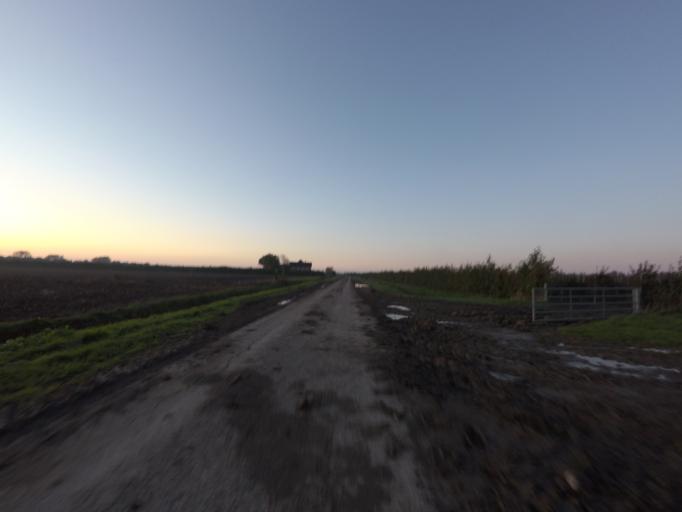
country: NL
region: North Brabant
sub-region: Gemeente Woudrichem
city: Almkerk
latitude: 51.7818
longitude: 4.9766
